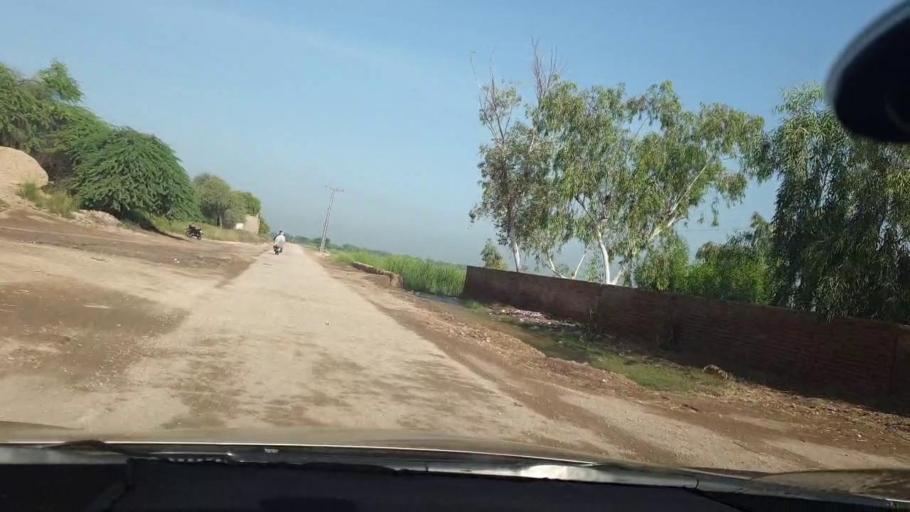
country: PK
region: Sindh
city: Kambar
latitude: 27.6554
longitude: 68.0303
